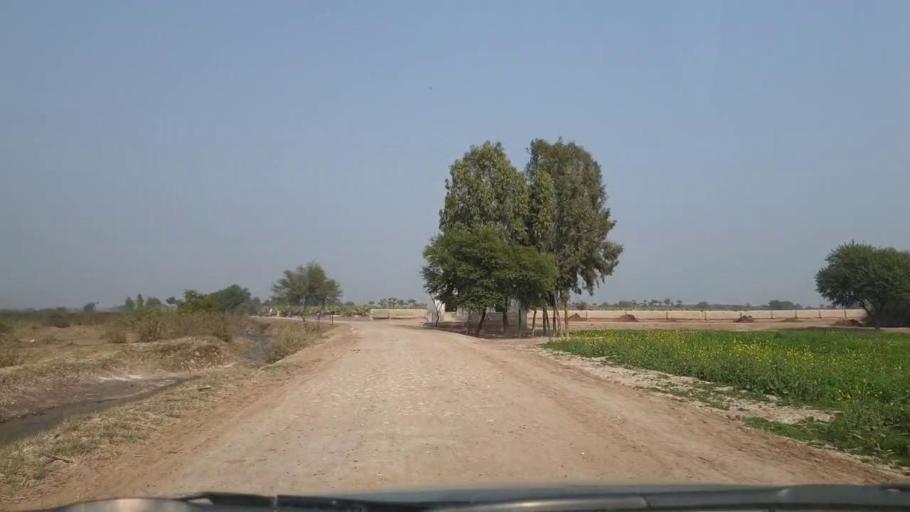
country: PK
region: Sindh
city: Matiari
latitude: 25.6577
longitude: 68.5432
